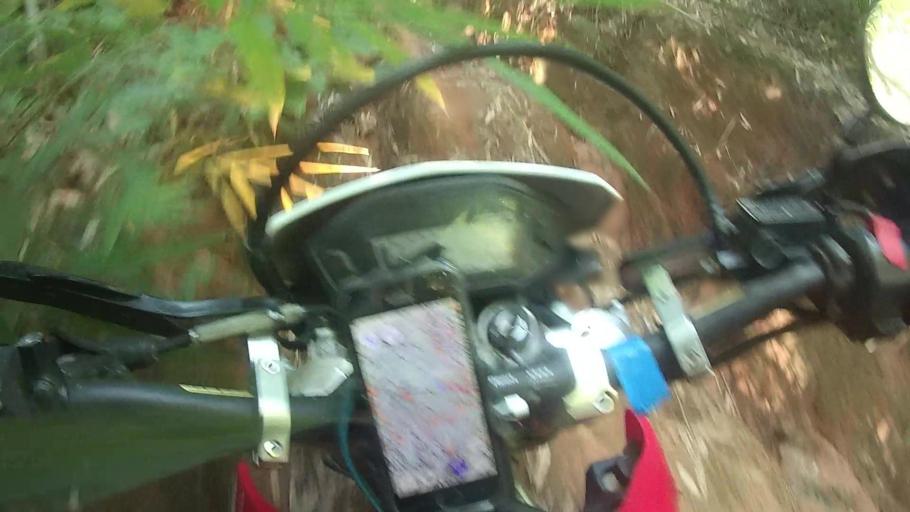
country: TH
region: Chiang Mai
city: Samoeng
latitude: 18.9242
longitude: 98.8783
